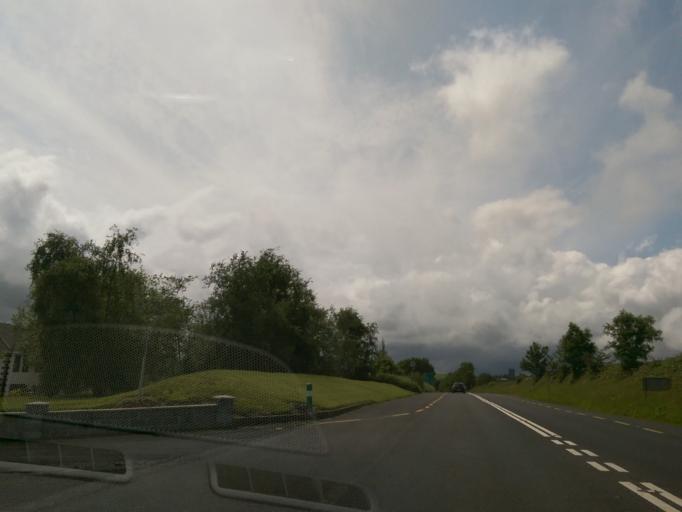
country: IE
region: Munster
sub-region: An Clar
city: Ennis
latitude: 52.8237
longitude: -9.0083
